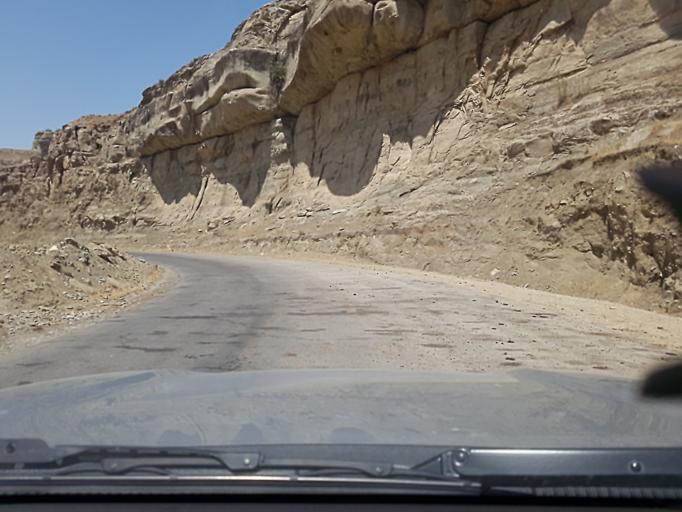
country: TM
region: Balkan
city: Magtymguly
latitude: 38.4228
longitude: 56.6521
